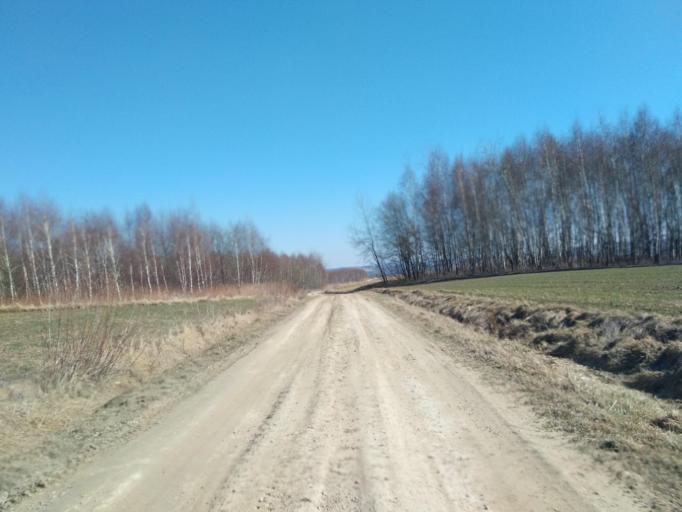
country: PL
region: Subcarpathian Voivodeship
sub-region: Powiat ropczycko-sedziszowski
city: Niedzwiada
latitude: 49.9531
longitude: 21.5595
